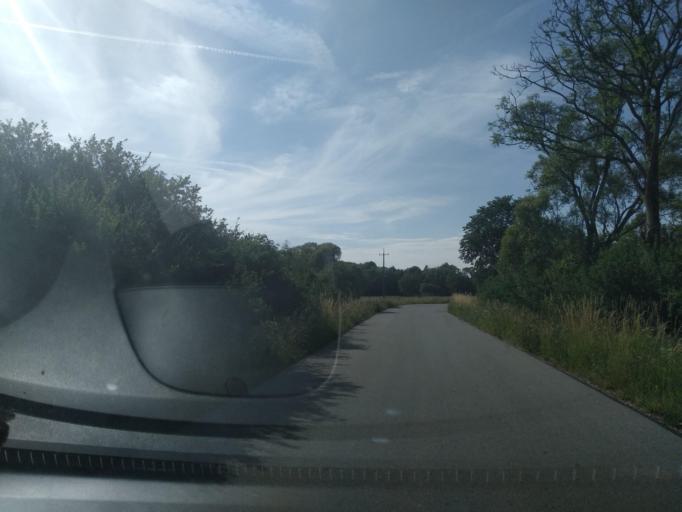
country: PL
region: Subcarpathian Voivodeship
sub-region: Powiat krosnienski
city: Jasliska
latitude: 49.4159
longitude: 21.8582
